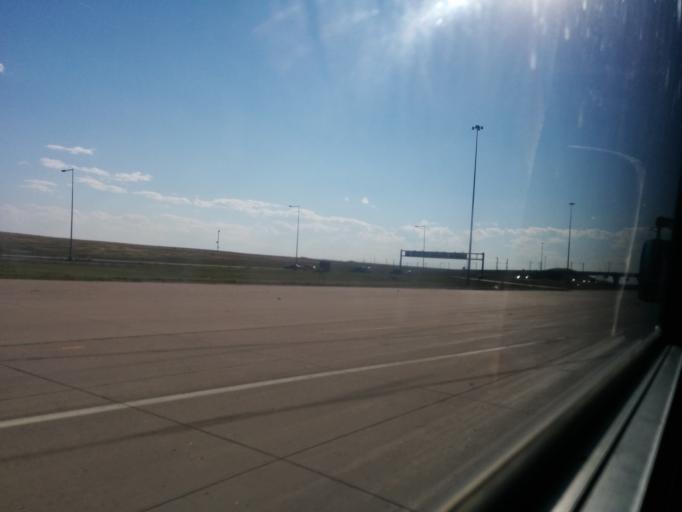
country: US
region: Colorado
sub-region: Adams County
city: Aurora
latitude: 39.8345
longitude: -104.7295
